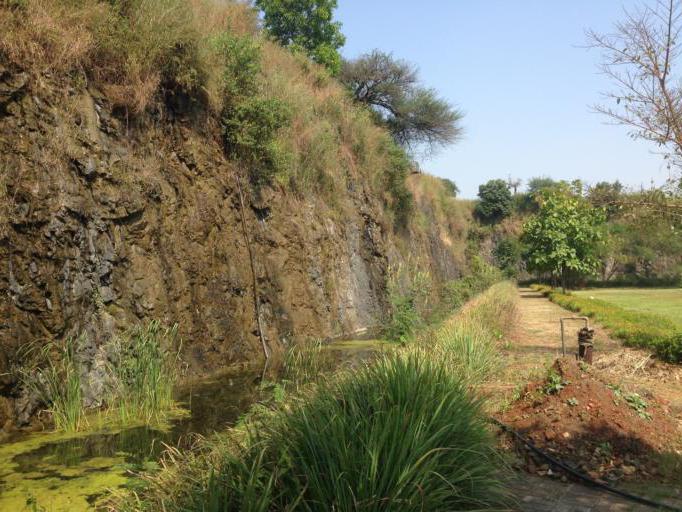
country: IN
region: Karnataka
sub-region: Belgaum
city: Belgaum
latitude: 15.8226
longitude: 74.4799
